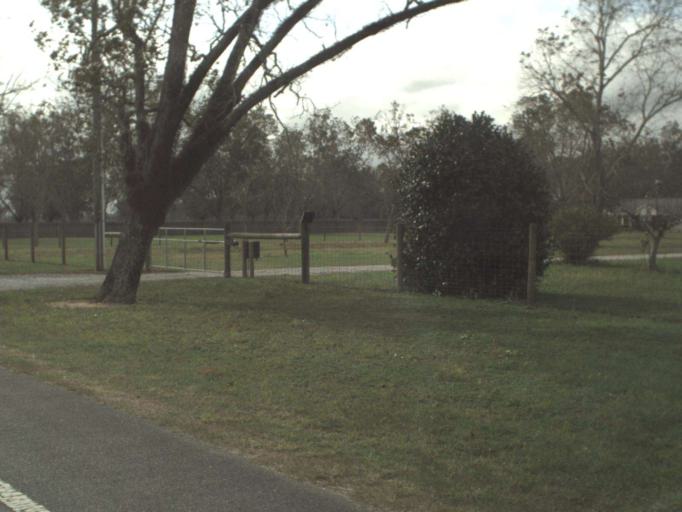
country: US
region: Florida
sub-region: Santa Rosa County
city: Point Baker
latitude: 30.7513
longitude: -87.0933
